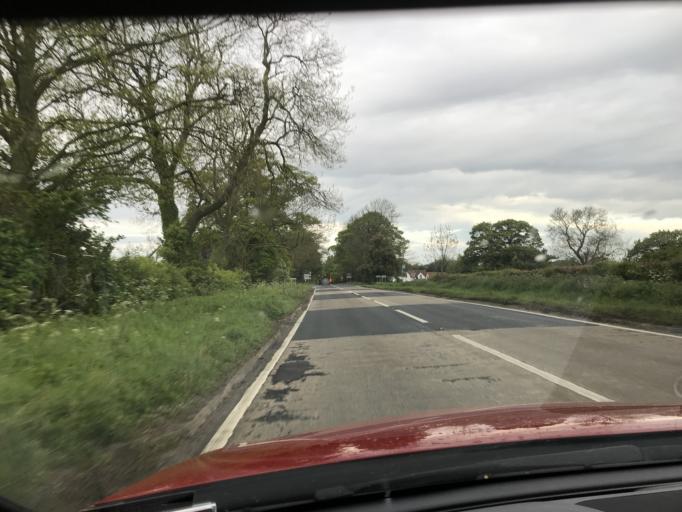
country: GB
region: England
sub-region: East Riding of Yorkshire
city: Cherry Burton
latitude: 53.8449
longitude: -0.4901
